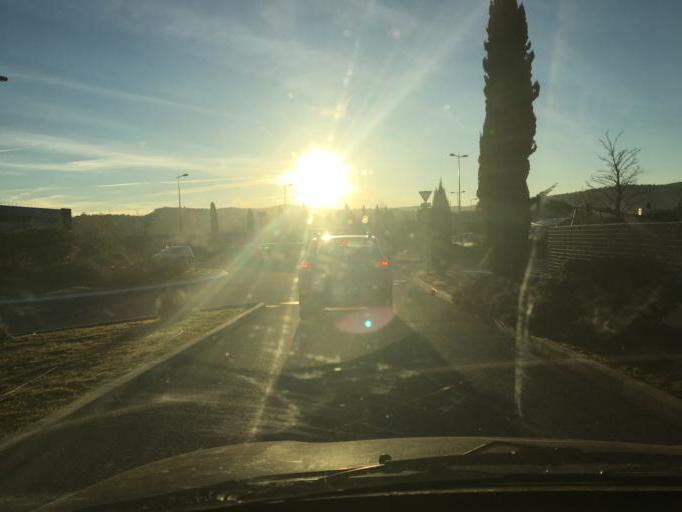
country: FR
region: Provence-Alpes-Cote d'Azur
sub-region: Departement du Var
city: Les Arcs
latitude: 43.4520
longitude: 6.4906
